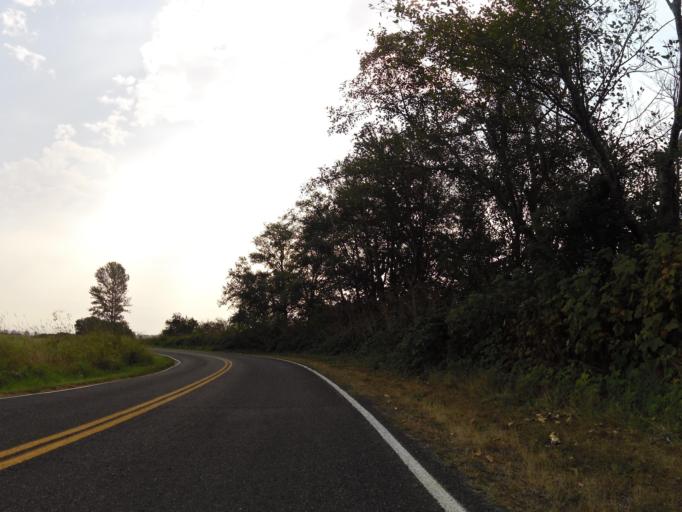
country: US
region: Washington
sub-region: Whatcom County
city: Ferndale
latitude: 48.8062
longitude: -122.6588
